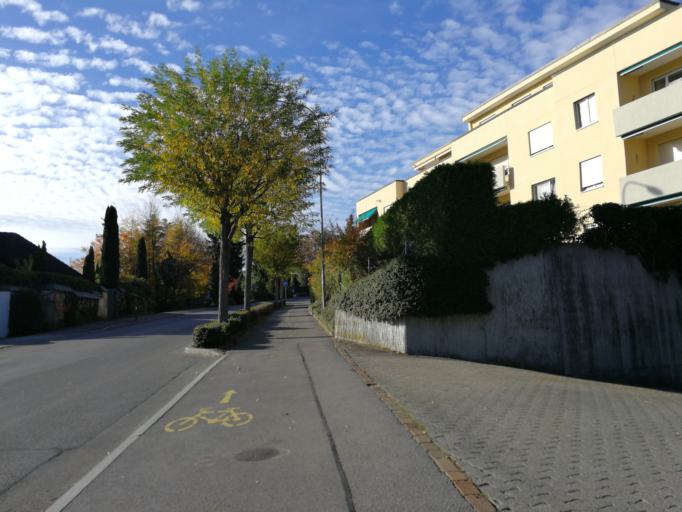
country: CH
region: Saint Gallen
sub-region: Wahlkreis See-Gaster
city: Rapperswil
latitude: 47.2402
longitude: 8.8212
